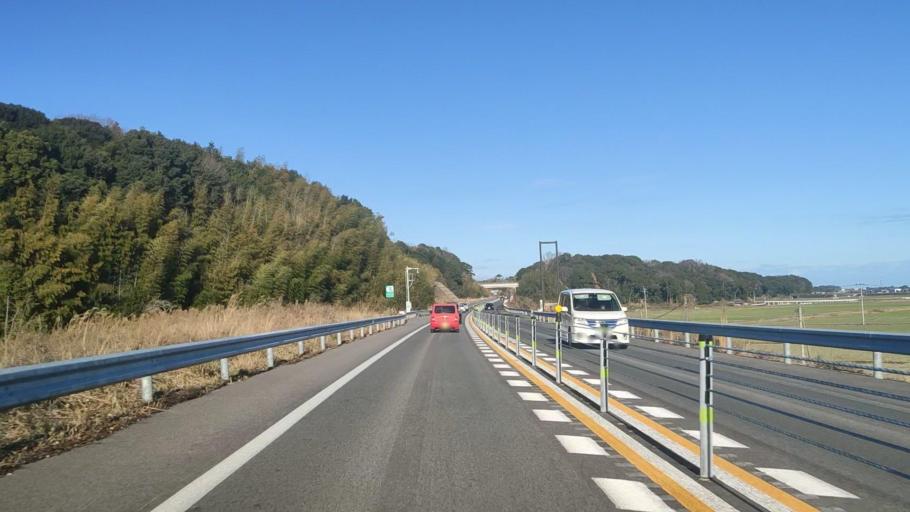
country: JP
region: Fukuoka
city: Nakatsu
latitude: 33.5501
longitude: 131.1833
